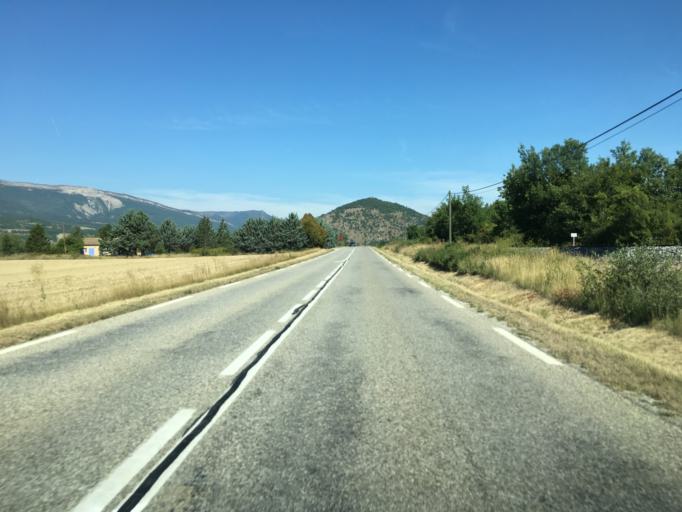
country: FR
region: Provence-Alpes-Cote d'Azur
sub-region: Departement des Hautes-Alpes
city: Laragne-Monteglin
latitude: 44.3638
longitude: 5.7583
